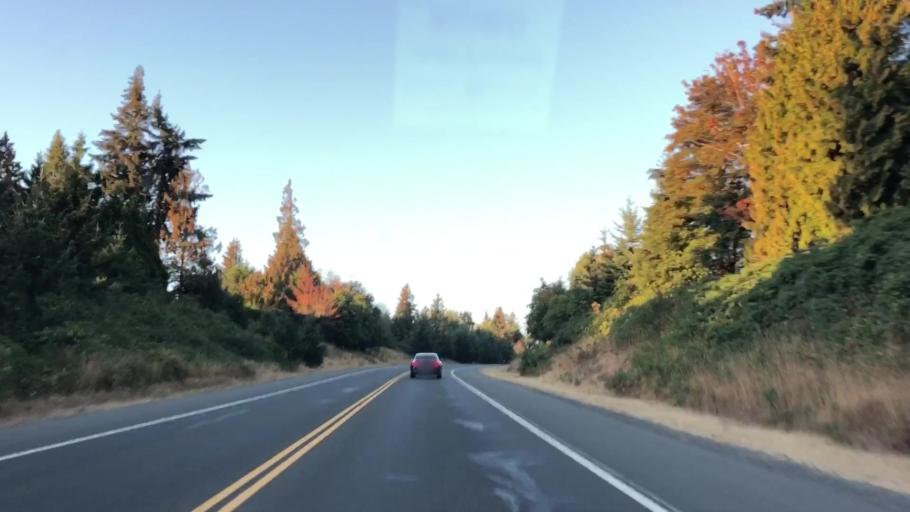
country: CA
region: British Columbia
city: Colwood
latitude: 48.4240
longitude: -123.5026
